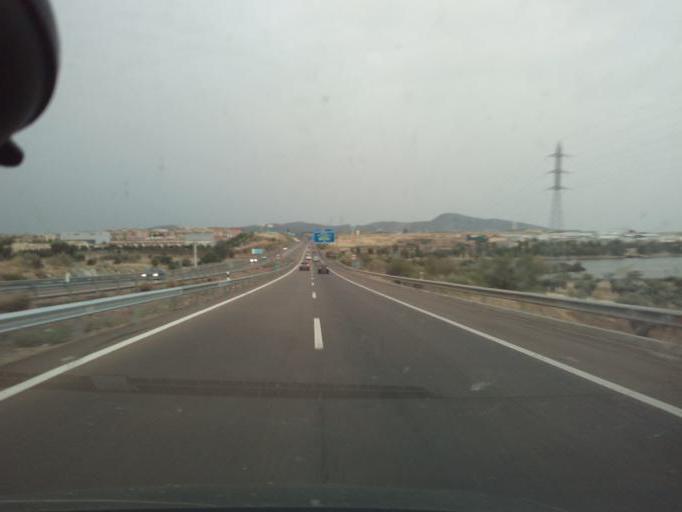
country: ES
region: Extremadura
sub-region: Provincia de Badajoz
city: Merida
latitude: 38.9327
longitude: -6.3668
